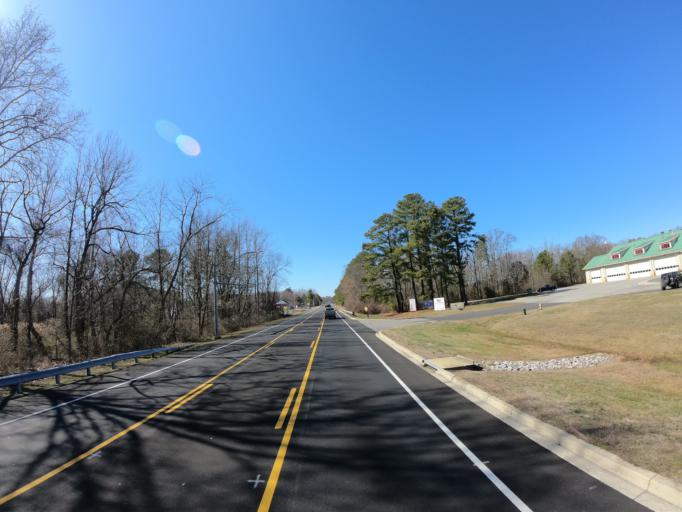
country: US
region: Maryland
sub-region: Kent County
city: Rock Hall
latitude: 39.1392
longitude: -76.2271
